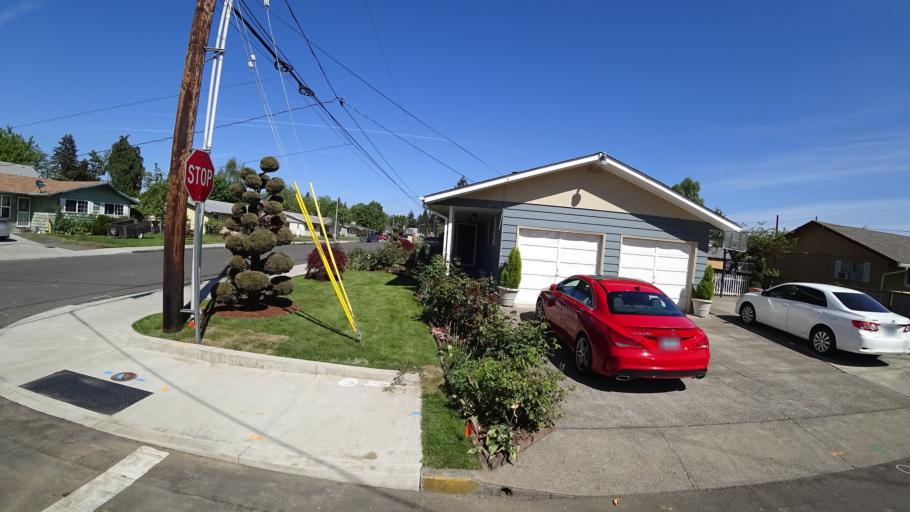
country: US
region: Oregon
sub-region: Washington County
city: Hillsboro
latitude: 45.5134
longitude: -122.9705
